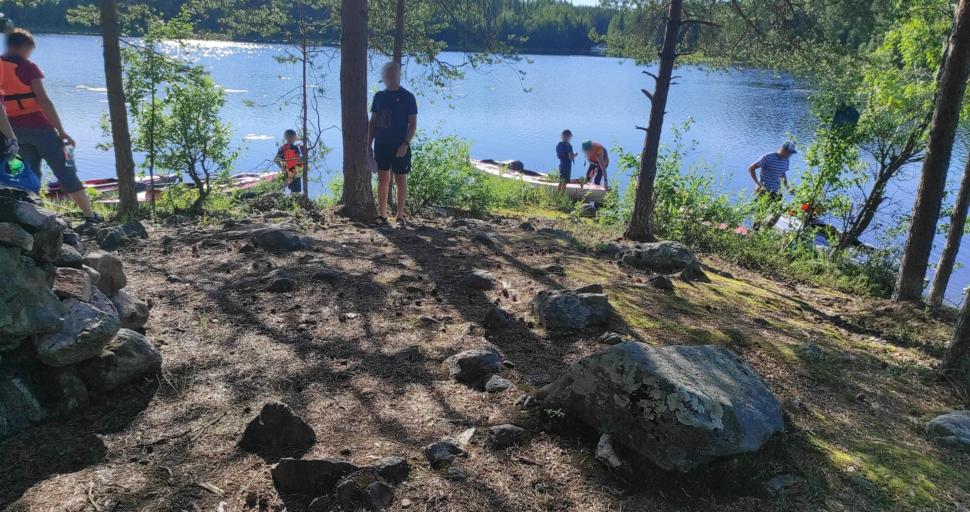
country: RU
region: Murmansk
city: Zelenoborskiy
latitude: 66.5704
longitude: 32.0792
